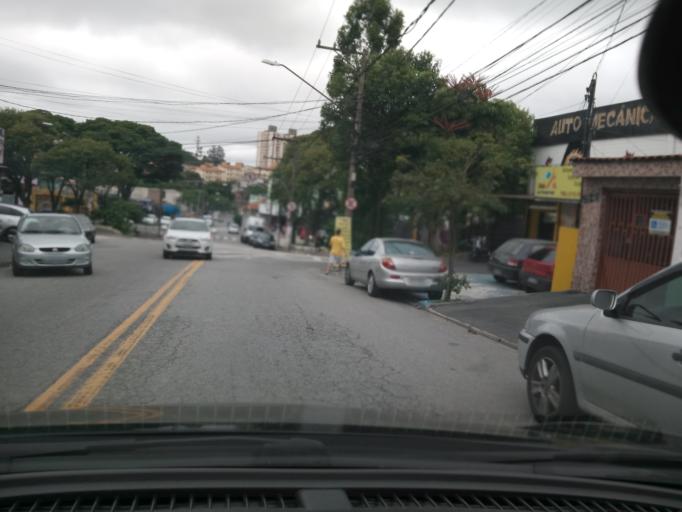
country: BR
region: Sao Paulo
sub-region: Sao Bernardo Do Campo
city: Sao Bernardo do Campo
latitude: -23.7193
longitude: -46.5830
